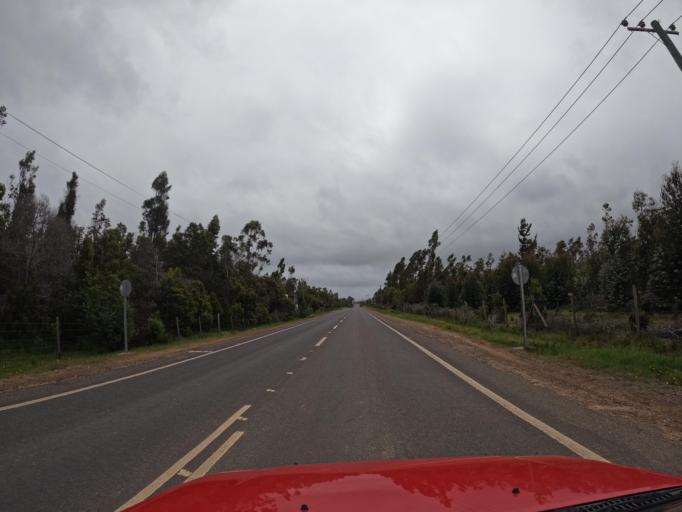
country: CL
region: O'Higgins
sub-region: Provincia de Colchagua
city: Santa Cruz
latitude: -34.5024
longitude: -72.0076
